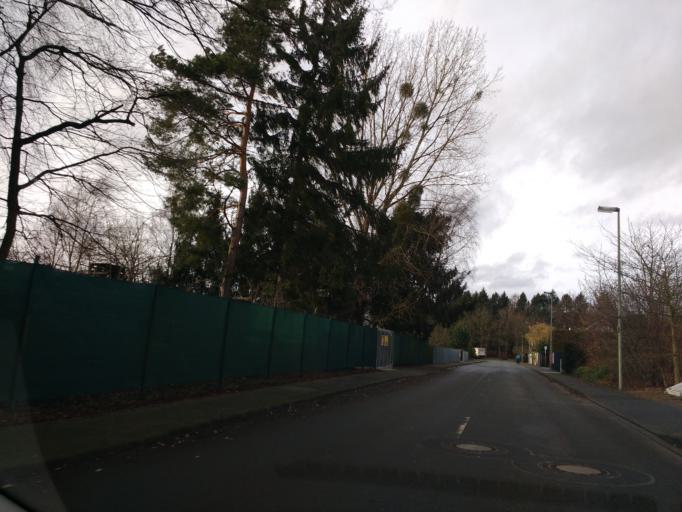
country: DE
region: North Rhine-Westphalia
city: Bad Lippspringe
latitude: 51.7807
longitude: 8.8006
